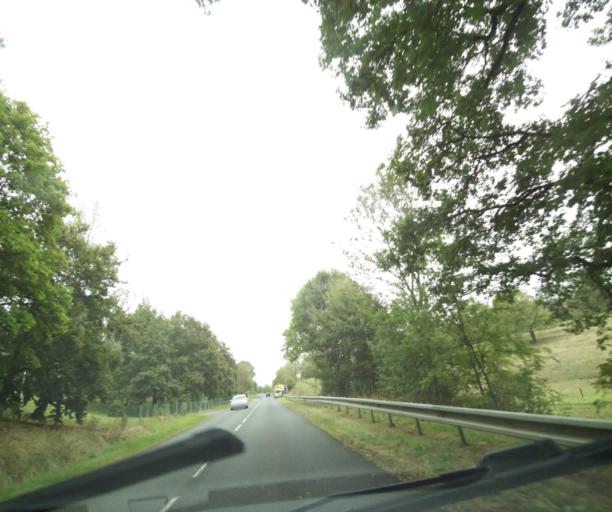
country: FR
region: Auvergne
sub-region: Departement du Puy-de-Dome
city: Saint-Genes-Champanelle
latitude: 45.7109
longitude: 3.0159
